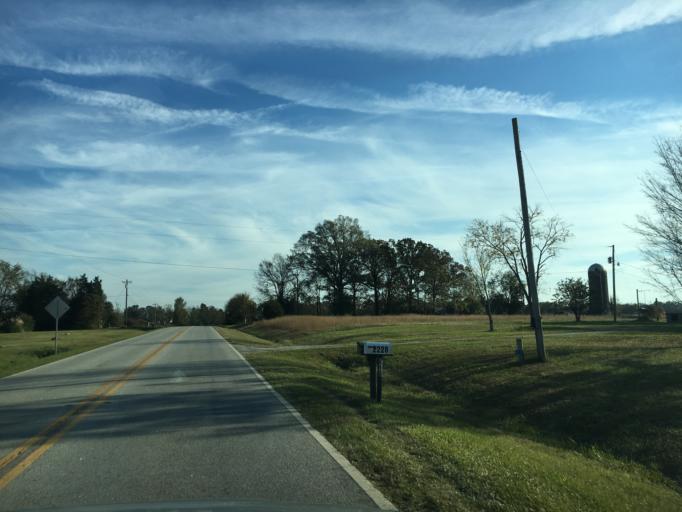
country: US
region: Georgia
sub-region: Elbert County
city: Elberton
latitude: 34.0386
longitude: -82.7975
